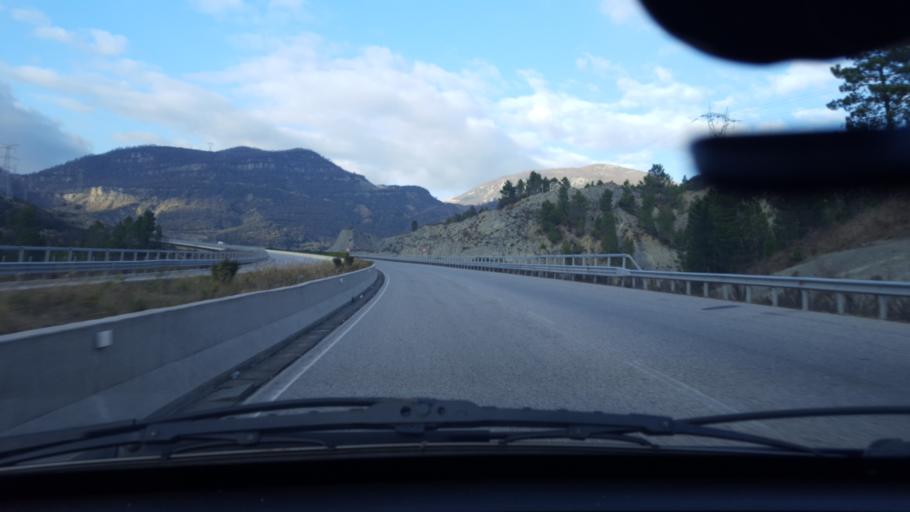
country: AL
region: Tirane
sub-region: Rrethi i Tiranes
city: Krrabe
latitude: 41.1847
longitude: 19.9950
